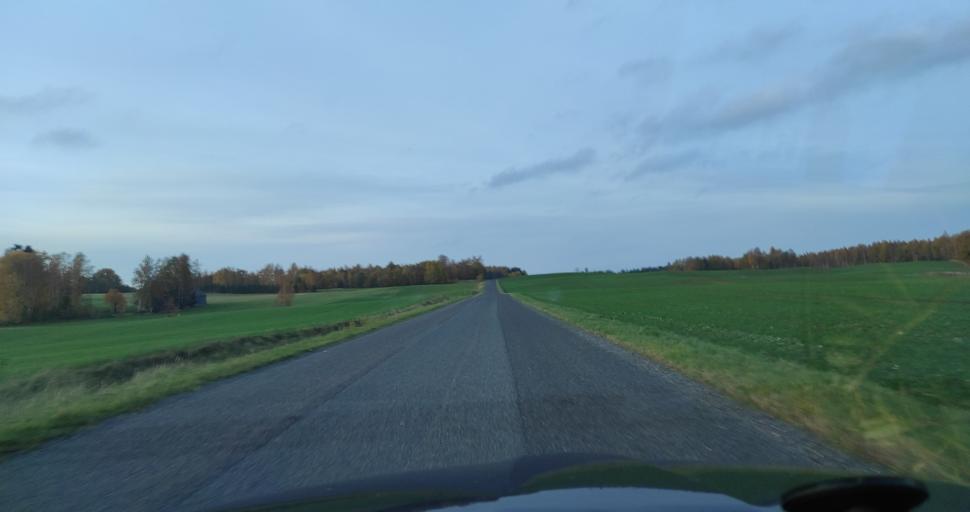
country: LV
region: Aizpute
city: Aizpute
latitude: 56.7021
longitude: 21.7948
